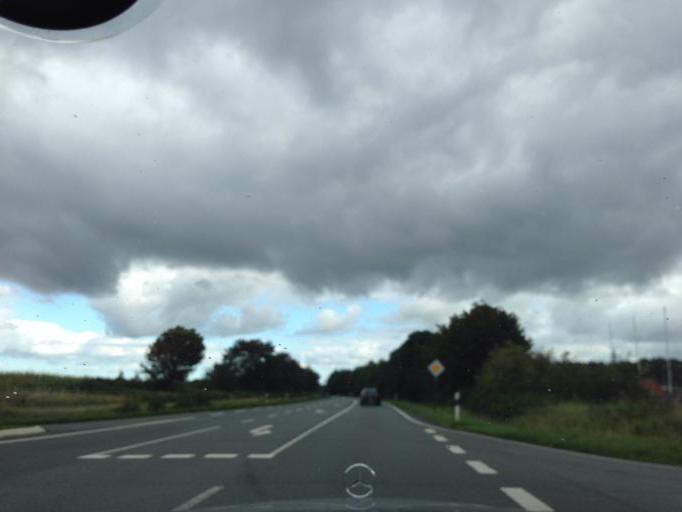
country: DE
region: Schleswig-Holstein
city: Horup
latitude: 54.7480
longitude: 9.1036
